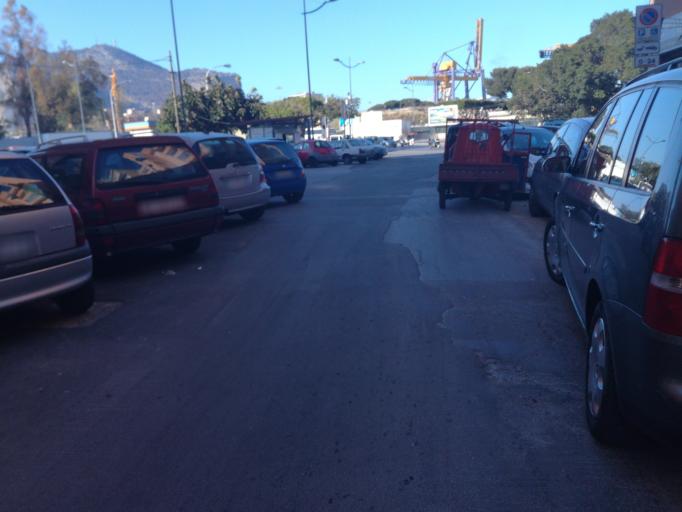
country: IT
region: Sicily
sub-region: Palermo
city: Palermo
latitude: 38.1302
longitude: 13.3599
